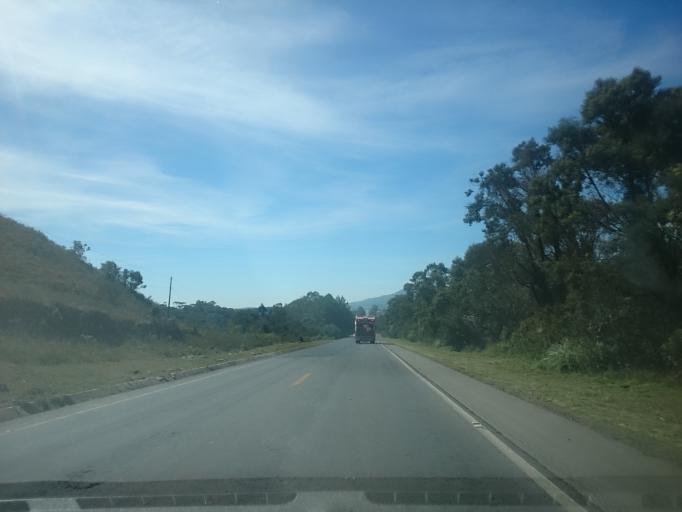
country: BR
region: Santa Catarina
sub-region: Lages
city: Lages
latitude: -27.7758
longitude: -50.2148
